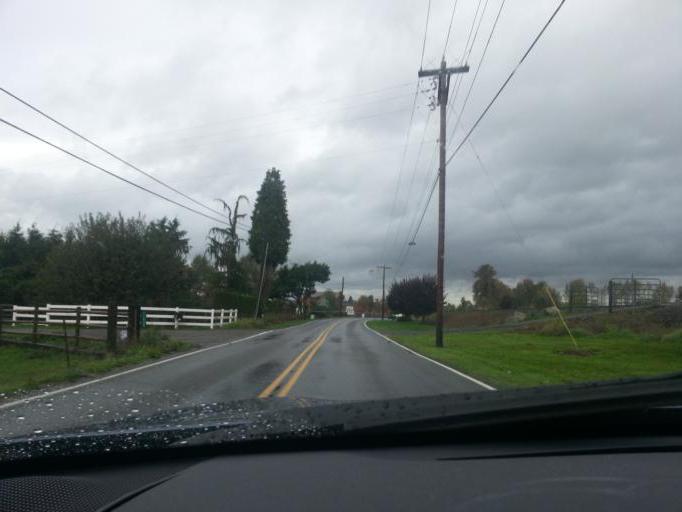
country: US
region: Washington
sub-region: Snohomish County
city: Snohomish
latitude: 47.8875
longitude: -122.0989
